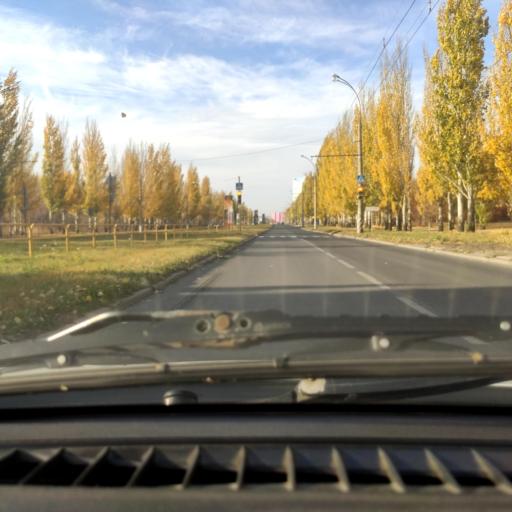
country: RU
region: Samara
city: Tol'yatti
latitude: 53.5474
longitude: 49.2743
